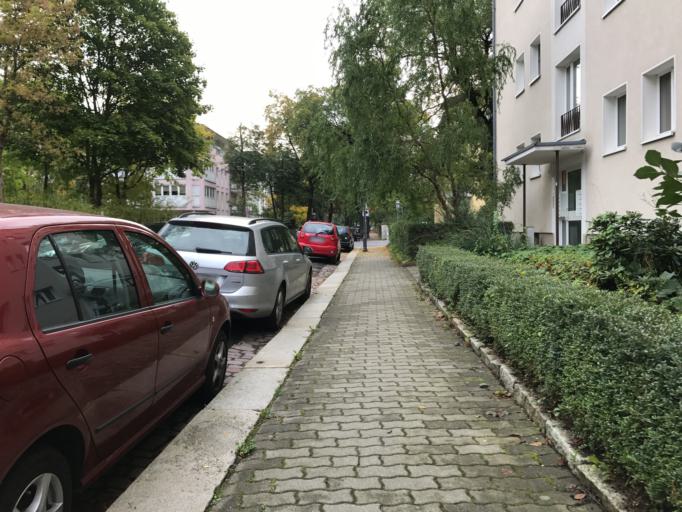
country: DE
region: Saxony
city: Albertstadt
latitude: 51.0509
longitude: 13.7891
